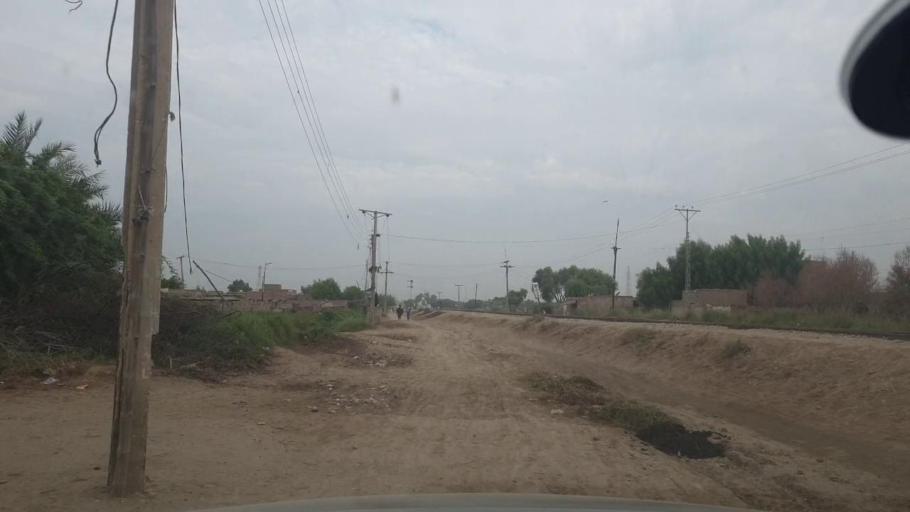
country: PK
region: Sindh
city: Jacobabad
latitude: 28.2659
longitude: 68.4440
